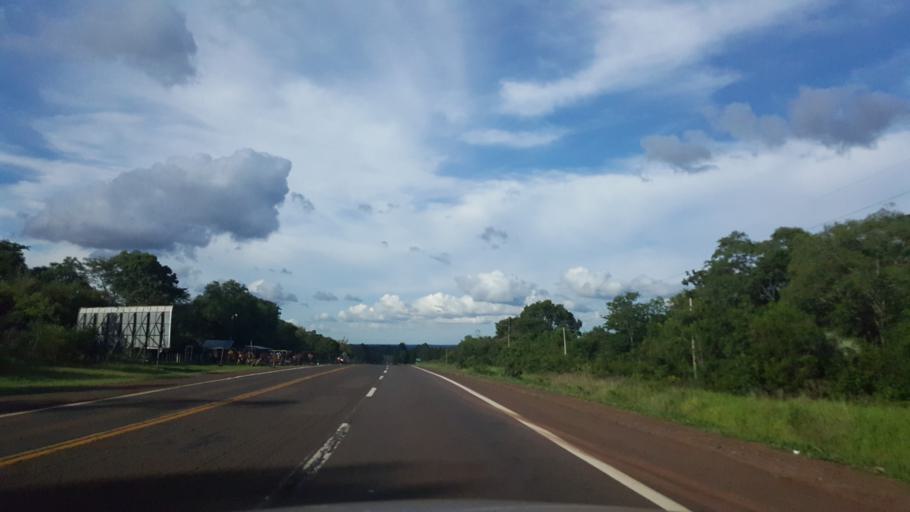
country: AR
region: Misiones
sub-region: Departamento de Candelaria
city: Loreto
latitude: -27.3499
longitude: -55.5479
